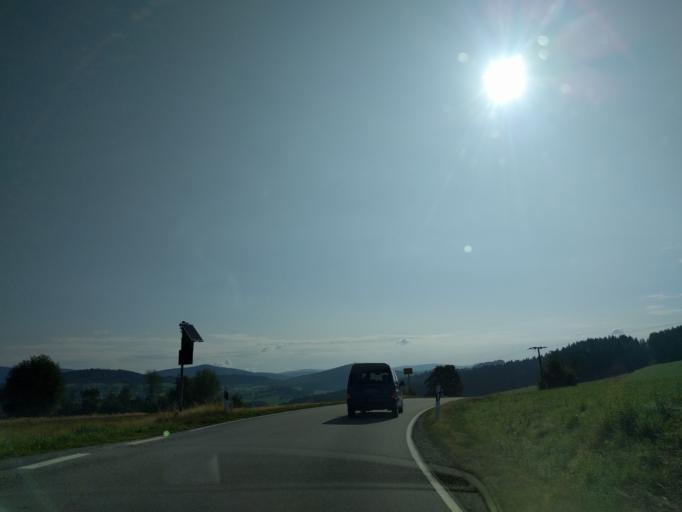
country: DE
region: Bavaria
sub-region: Lower Bavaria
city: Neuschonau
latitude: 48.8601
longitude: 13.4519
